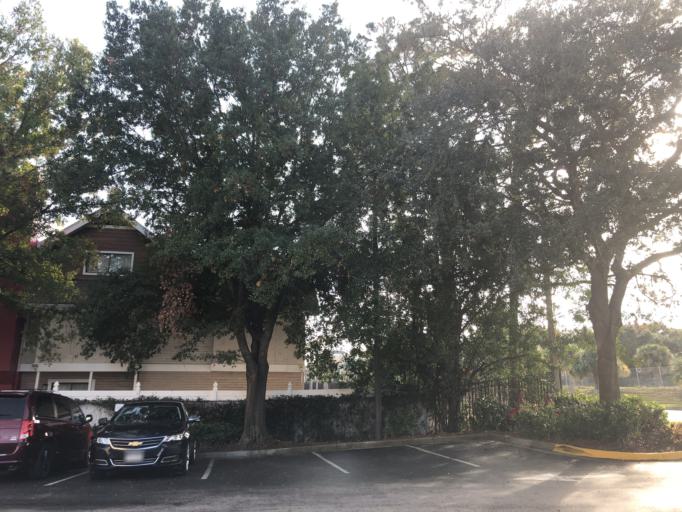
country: US
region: Florida
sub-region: Orange County
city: Tangelo Park
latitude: 28.4519
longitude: -81.4680
